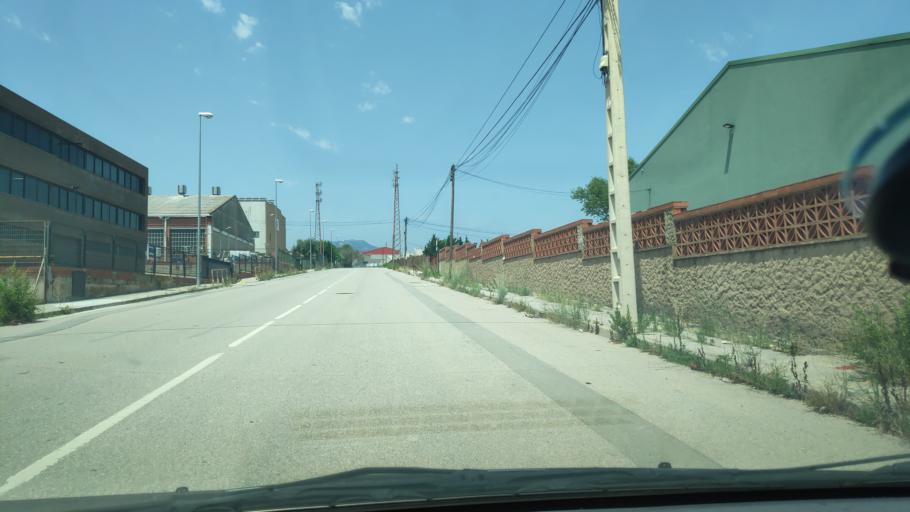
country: ES
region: Catalonia
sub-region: Provincia de Barcelona
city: Terrassa
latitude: 41.5489
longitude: 2.0367
